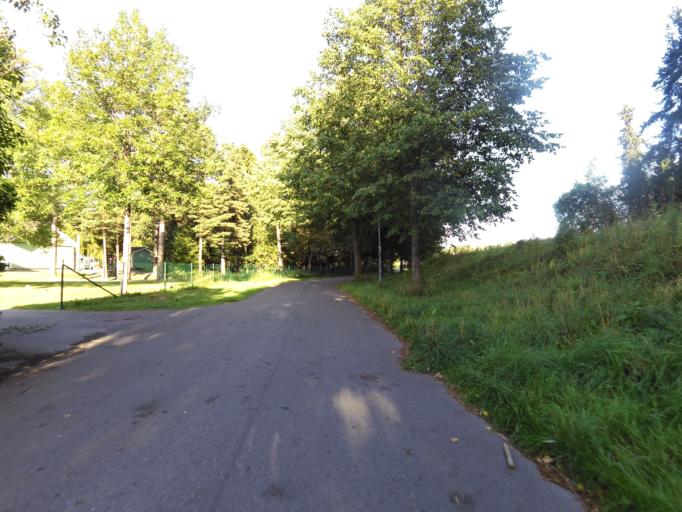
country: SE
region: Gaevleborg
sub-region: Gavle Kommun
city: Gavle
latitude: 60.6497
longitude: 17.1383
